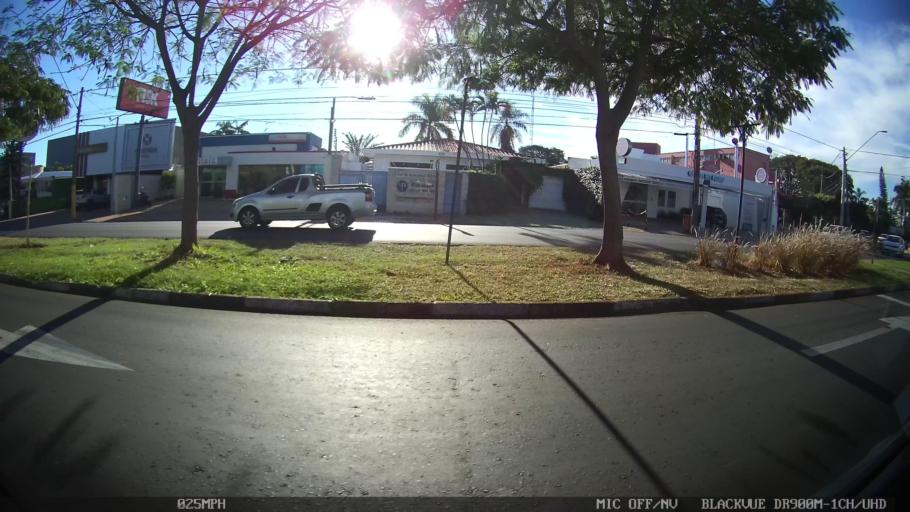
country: BR
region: Sao Paulo
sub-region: Araraquara
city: Araraquara
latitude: -21.7746
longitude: -48.1746
